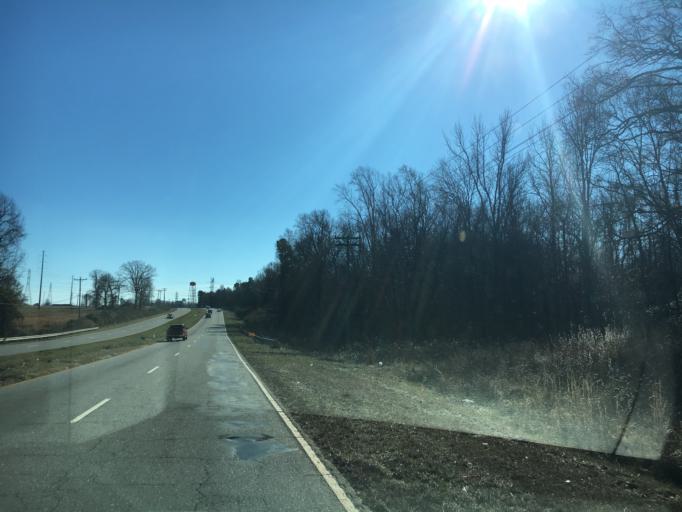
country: US
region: South Carolina
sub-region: Anderson County
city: Homeland Park
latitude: 34.4468
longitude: -82.6685
